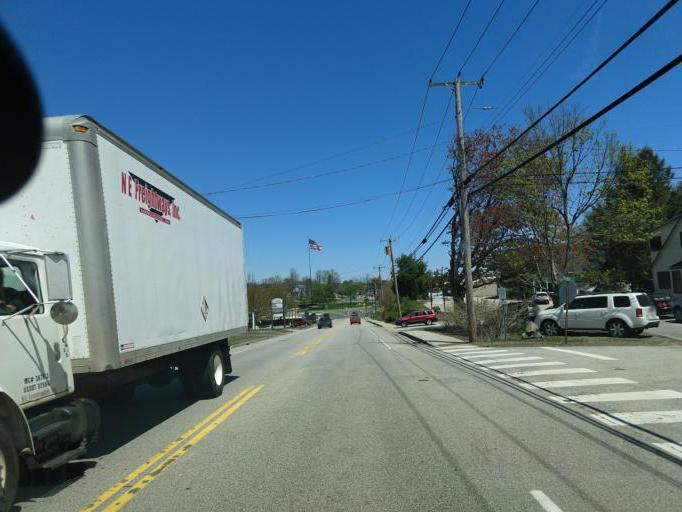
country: US
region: Maine
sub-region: York County
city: Kittery
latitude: 43.0983
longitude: -70.7450
